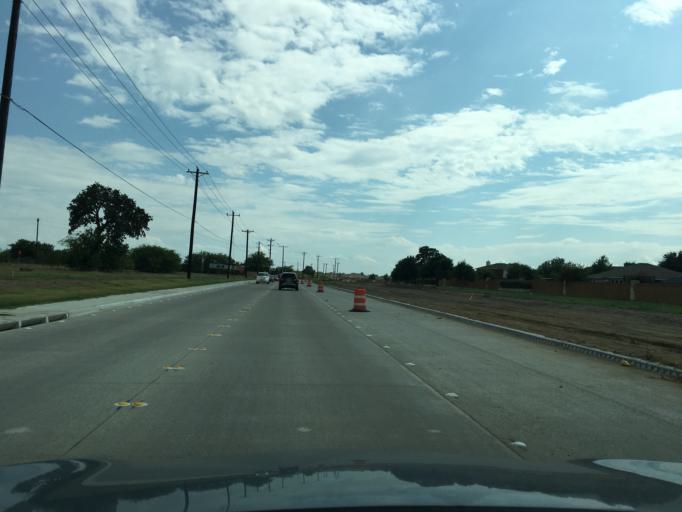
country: US
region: Texas
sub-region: Denton County
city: Oak Point
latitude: 33.2057
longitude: -96.9763
